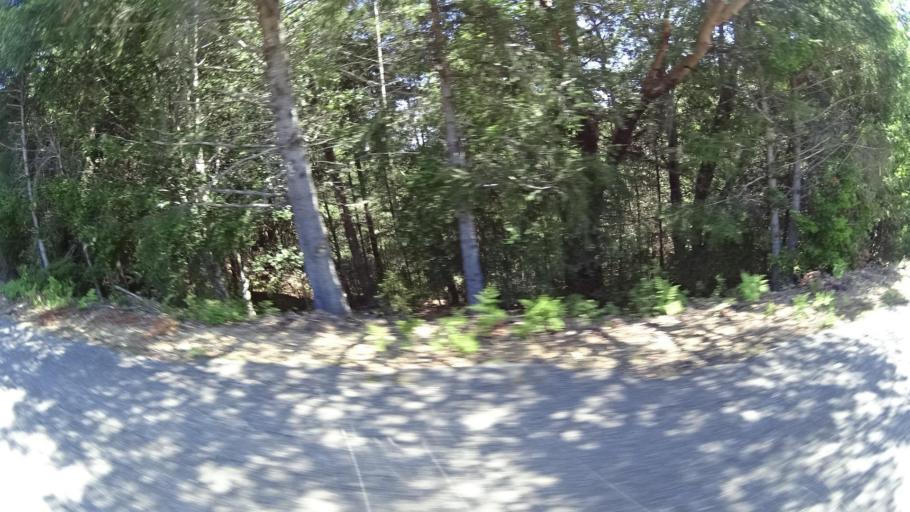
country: US
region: California
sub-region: Humboldt County
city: Redway
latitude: 40.1548
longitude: -124.0454
